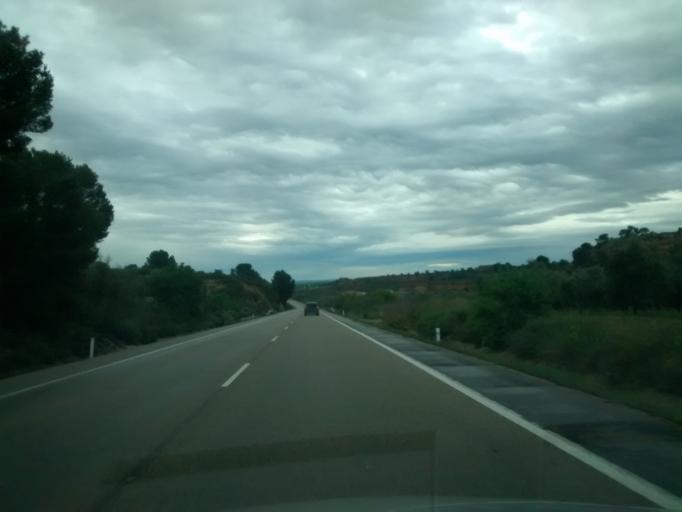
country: ES
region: Aragon
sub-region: Provincia de Zaragoza
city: Maella
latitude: 41.1673
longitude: 0.0749
